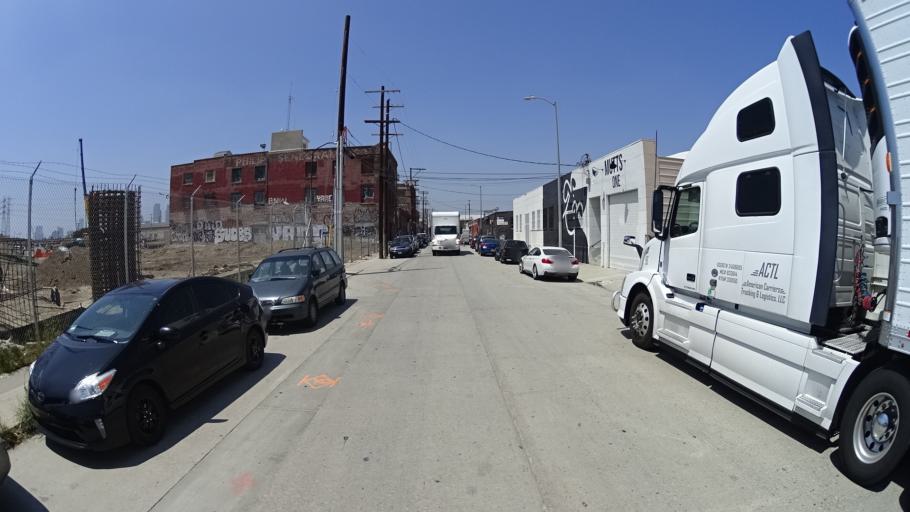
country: US
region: California
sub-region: Los Angeles County
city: Boyle Heights
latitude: 34.0378
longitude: -118.2235
